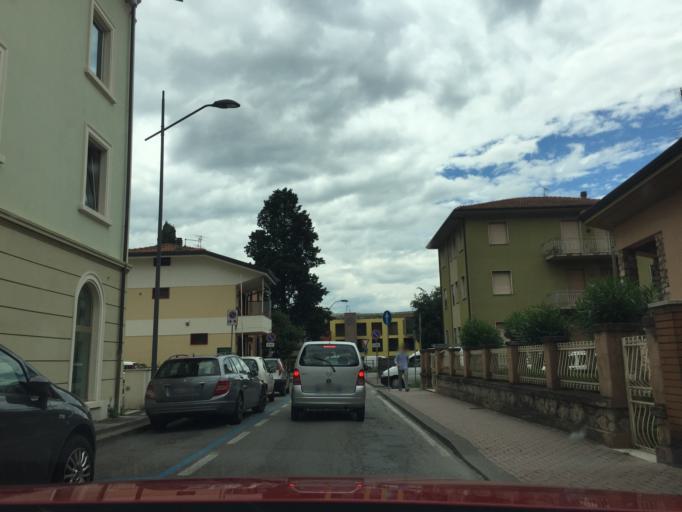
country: IT
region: Tuscany
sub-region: Provincia di Pistoia
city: Montecatini-Terme
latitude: 43.8791
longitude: 10.7752
